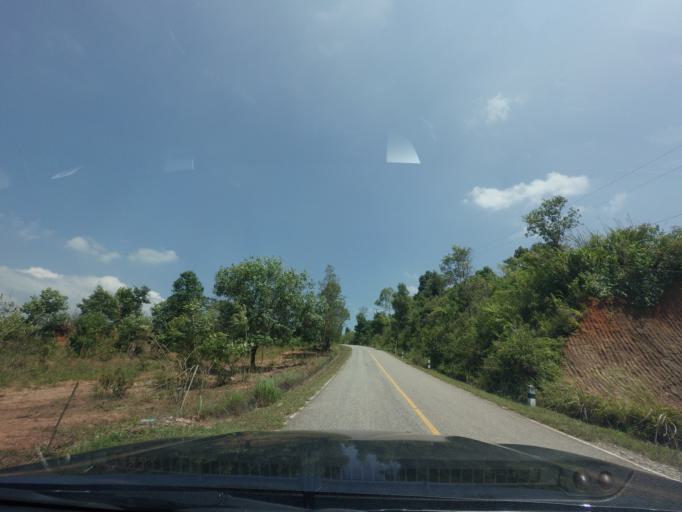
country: TH
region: Loei
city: Na Haeo
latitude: 17.5869
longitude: 100.9075
